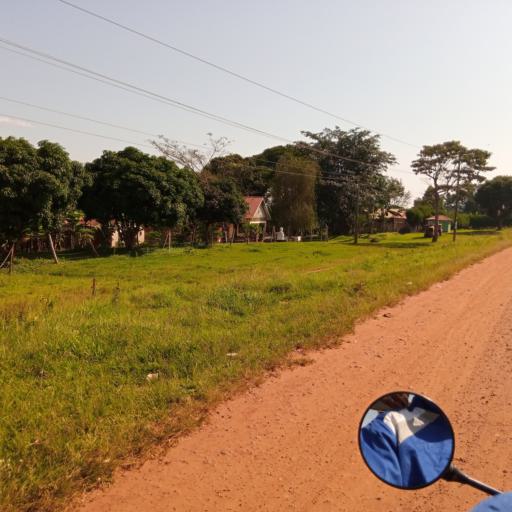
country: UG
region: Central Region
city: Masaka
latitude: -0.3805
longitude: 31.7047
